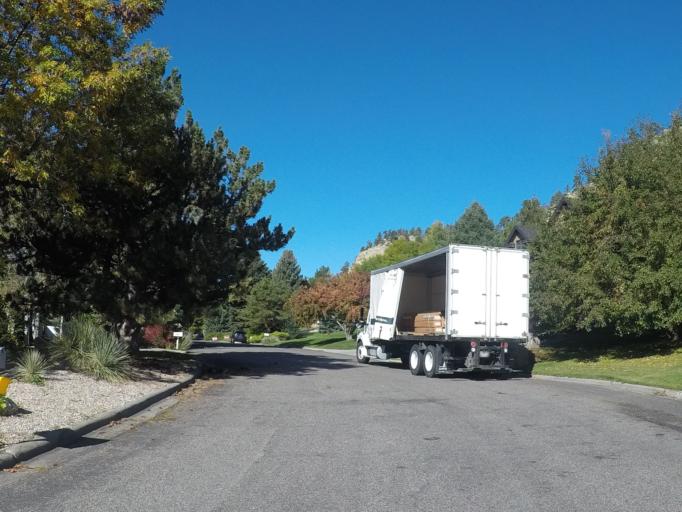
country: US
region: Montana
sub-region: Yellowstone County
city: Billings
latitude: 45.8013
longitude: -108.5838
